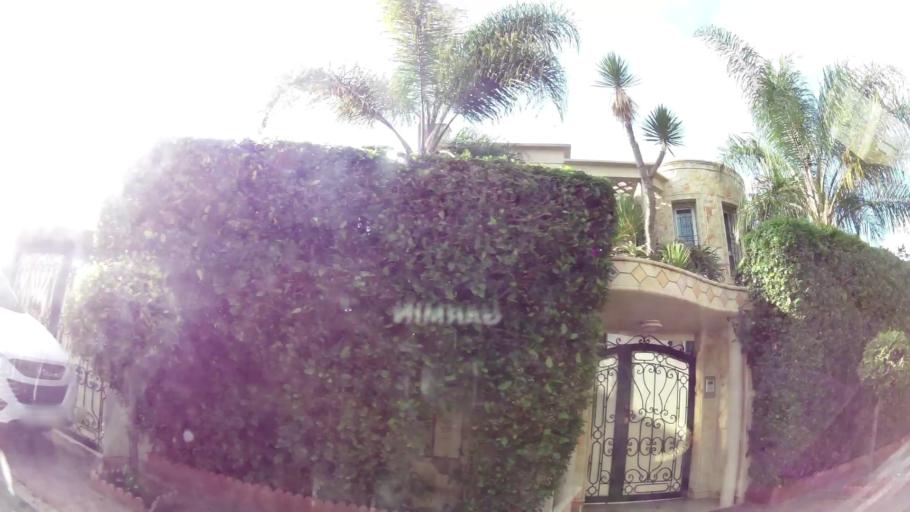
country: MA
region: Rabat-Sale-Zemmour-Zaer
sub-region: Skhirate-Temara
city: Temara
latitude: 33.9514
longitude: -6.8583
